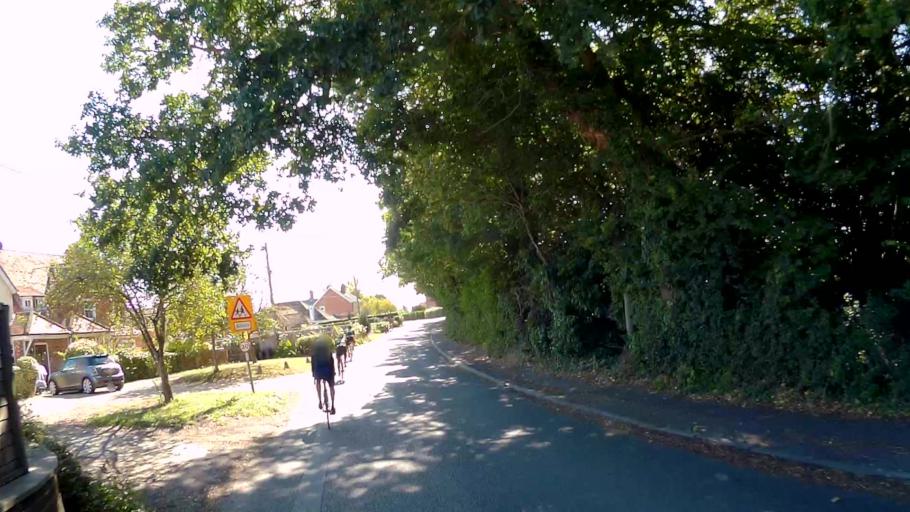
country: GB
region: England
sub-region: Wokingham
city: Swallowfield
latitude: 51.3870
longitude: -0.9774
